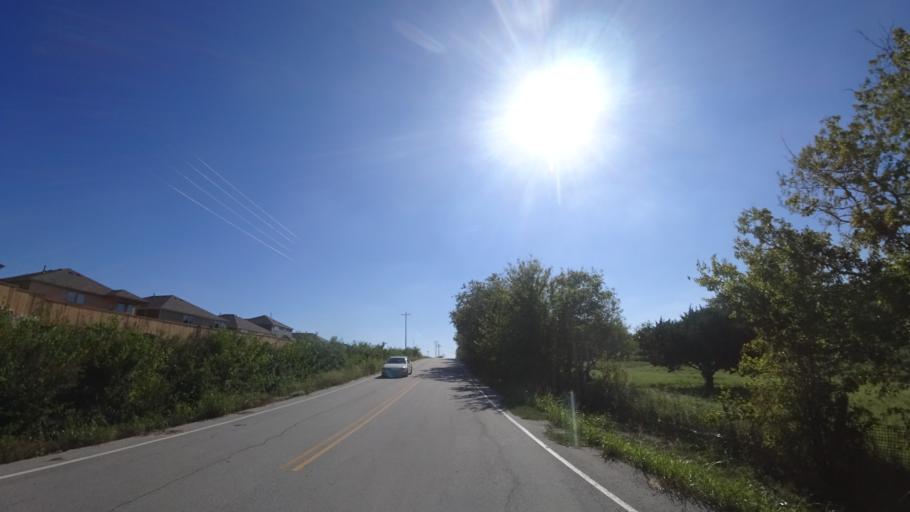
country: US
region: Texas
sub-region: Travis County
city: Manor
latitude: 30.3586
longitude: -97.6063
